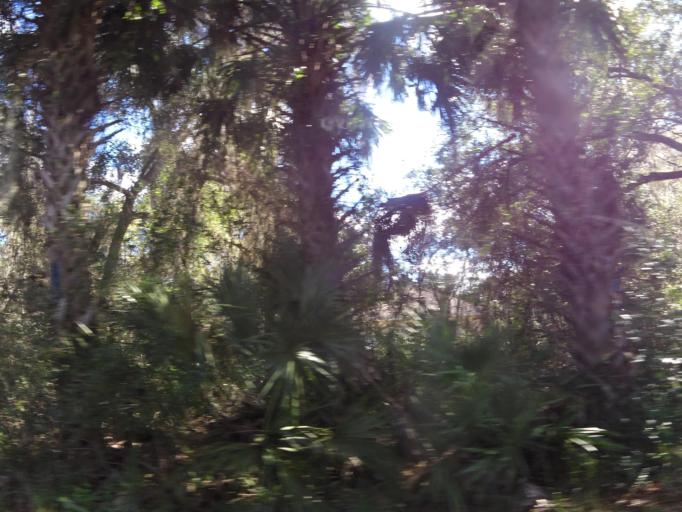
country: US
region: Florida
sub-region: Volusia County
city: Orange City
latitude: 28.9509
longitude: -81.3155
